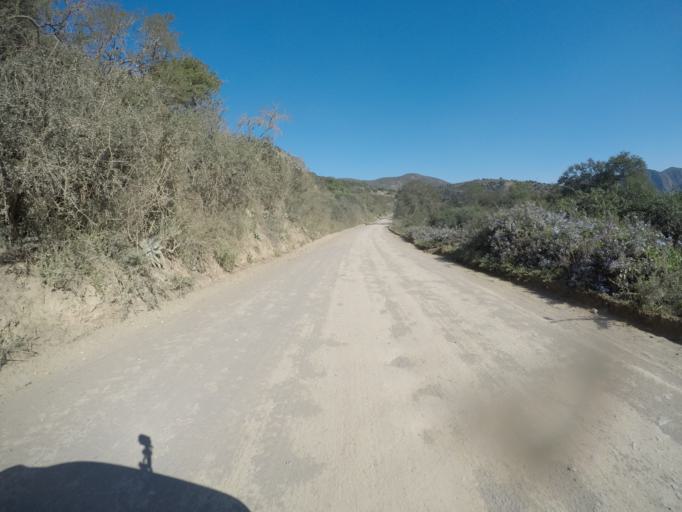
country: ZA
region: Eastern Cape
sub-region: Cacadu District Municipality
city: Kruisfontein
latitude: -33.6710
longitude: 24.5737
